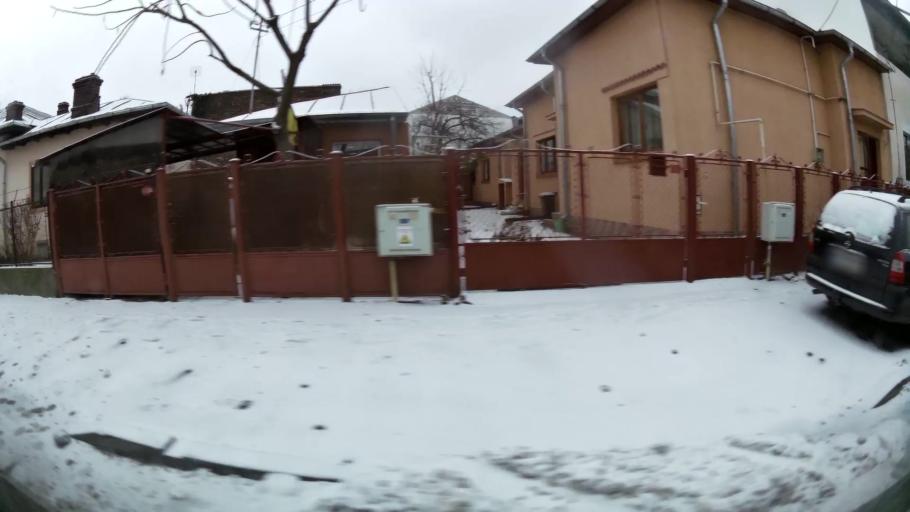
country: RO
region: Prahova
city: Ploiesti
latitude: 44.9361
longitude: 26.0377
